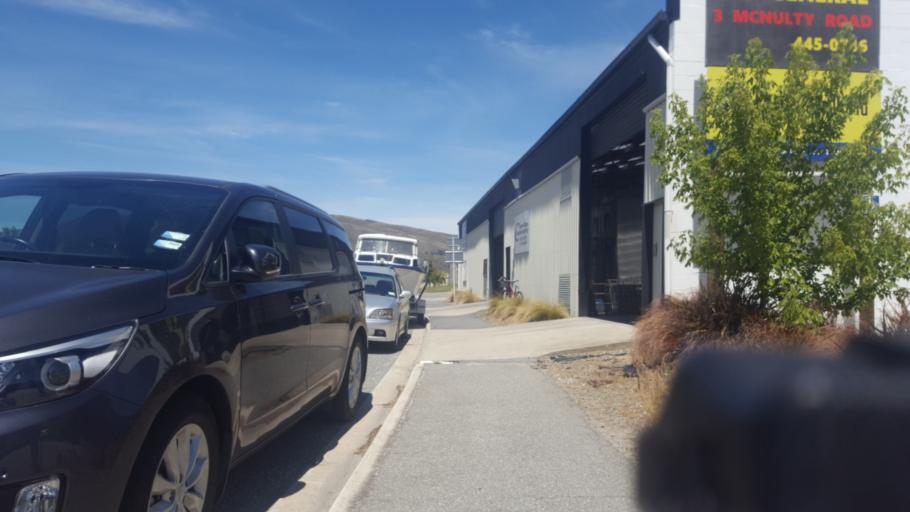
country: NZ
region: Otago
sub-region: Queenstown-Lakes District
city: Wanaka
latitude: -45.0488
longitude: 169.1945
